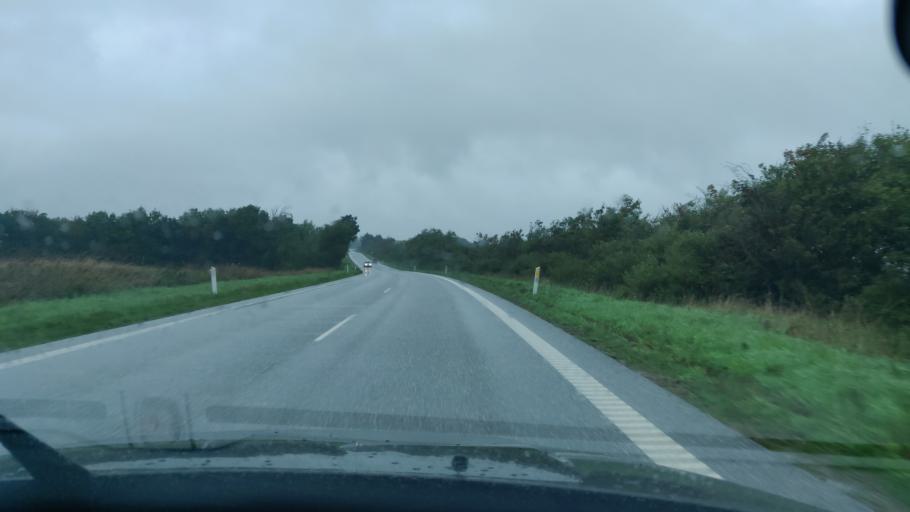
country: DK
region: North Denmark
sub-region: Thisted Kommune
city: Hurup
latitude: 56.8272
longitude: 8.5016
